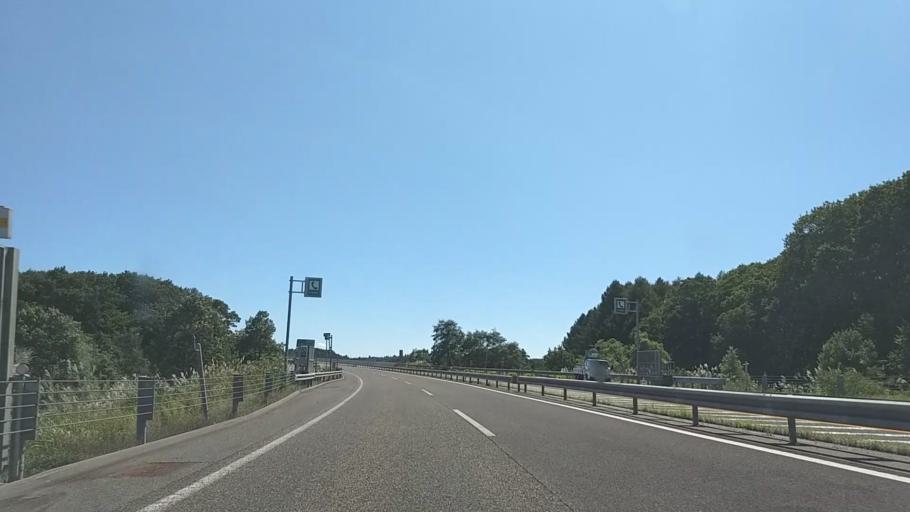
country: JP
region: Niigata
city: Arai
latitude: 36.8288
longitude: 138.1856
